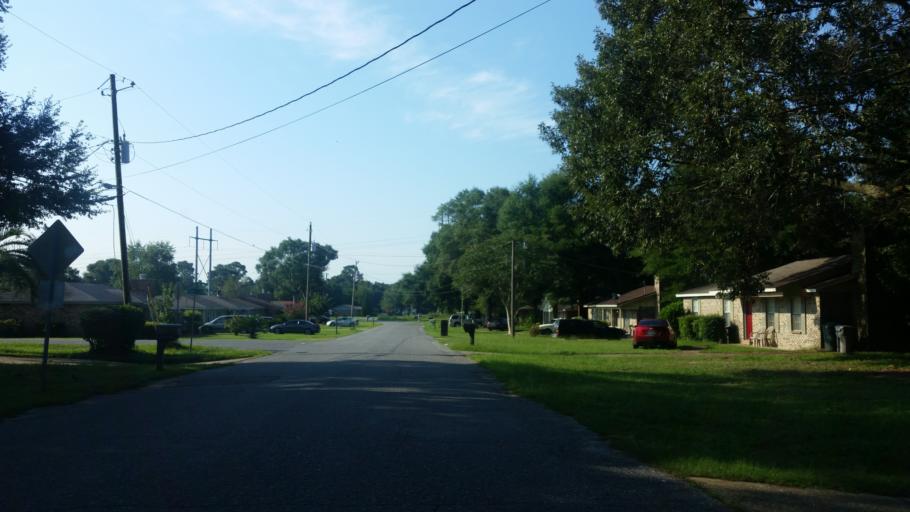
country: US
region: Florida
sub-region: Escambia County
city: Bellview
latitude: 30.4723
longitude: -87.2943
